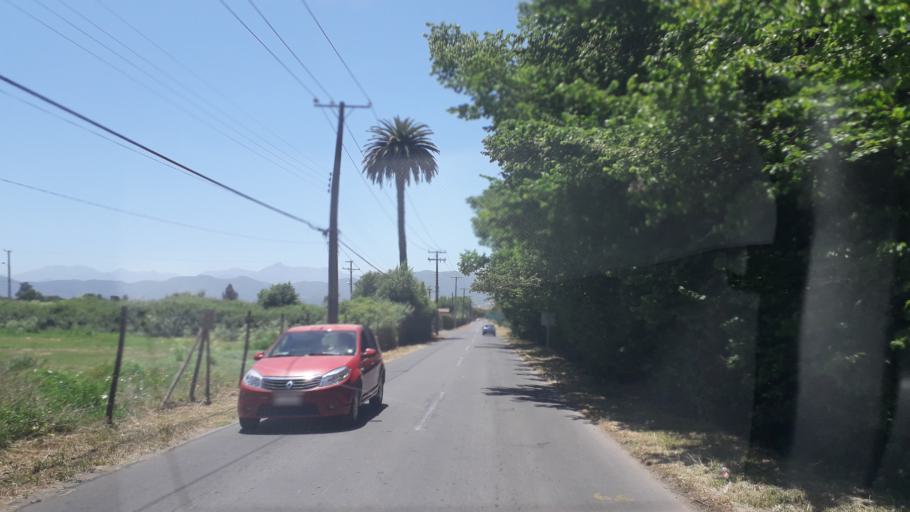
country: CL
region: Valparaiso
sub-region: Provincia de Quillota
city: Quillota
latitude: -32.9115
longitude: -71.2276
